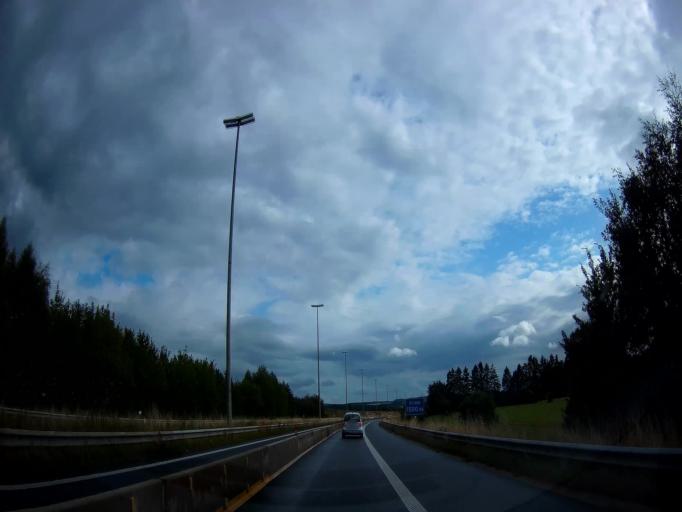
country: BE
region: Wallonia
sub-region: Province de Liege
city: Saint-Vith
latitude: 50.2838
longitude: 6.1070
